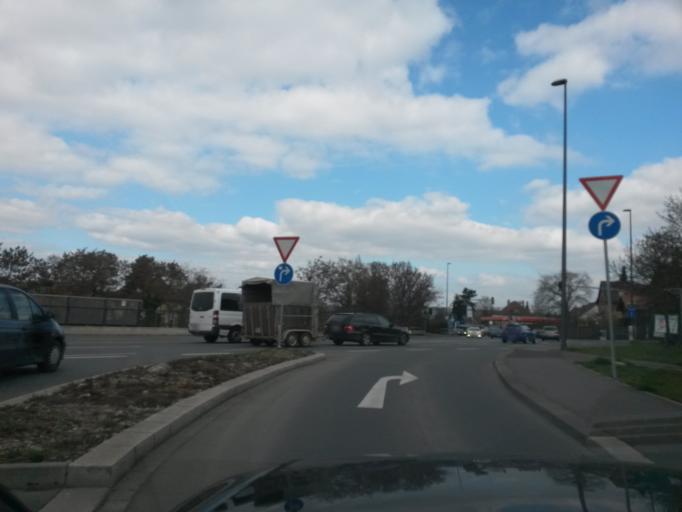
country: DE
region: Bavaria
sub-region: Regierungsbezirk Unterfranken
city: Wuerzburg
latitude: 49.7766
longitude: 9.9430
